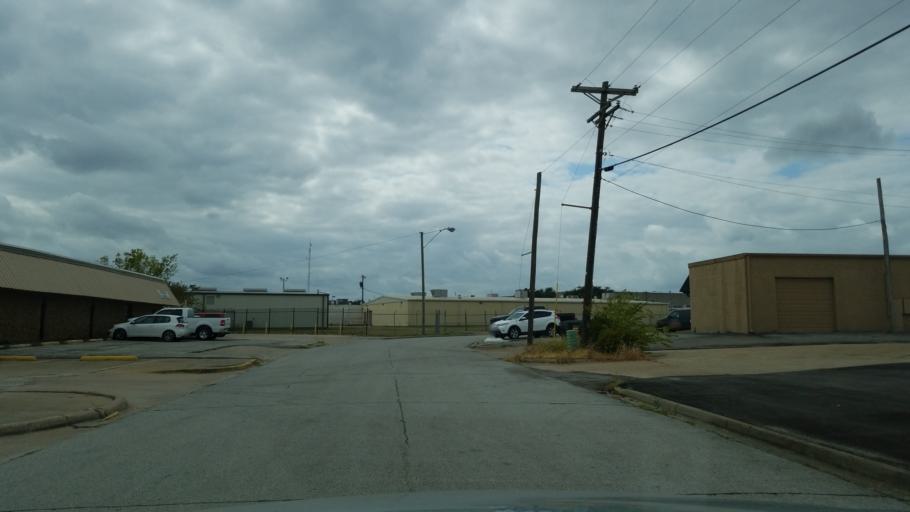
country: US
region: Texas
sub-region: Dallas County
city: Garland
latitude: 32.8834
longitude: -96.6714
